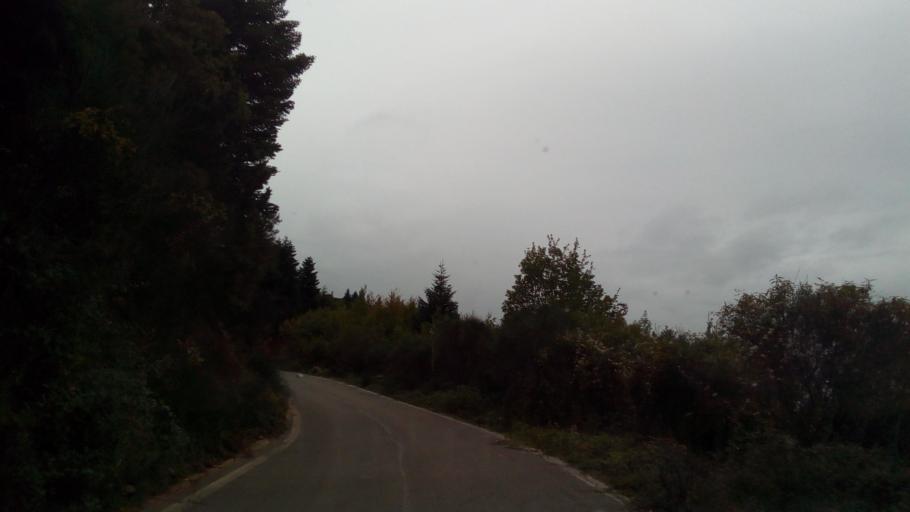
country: GR
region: West Greece
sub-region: Nomos Aitolias kai Akarnanias
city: Thermo
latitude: 38.5924
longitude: 21.8516
